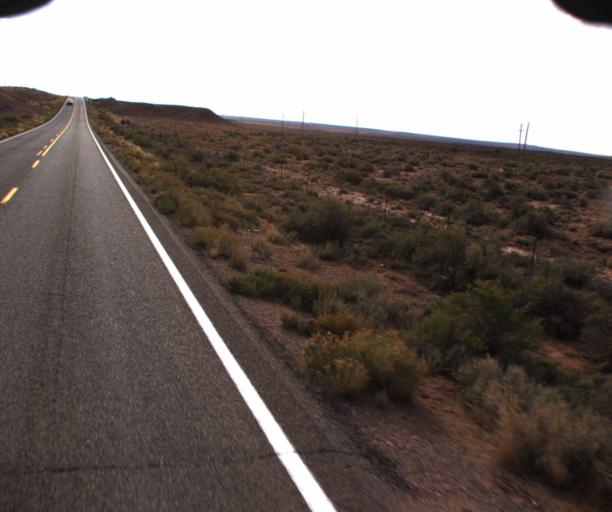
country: US
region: Arizona
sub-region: Apache County
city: Many Farms
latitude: 36.5273
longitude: -109.5018
